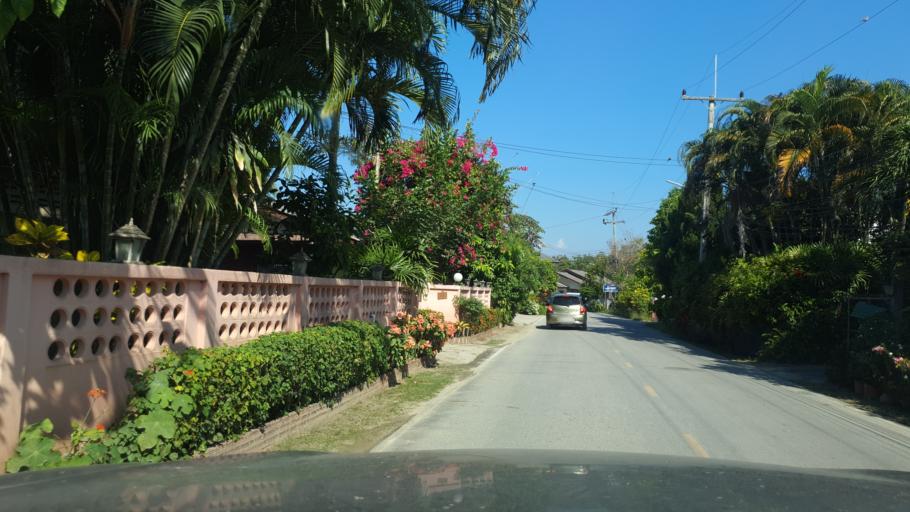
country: TH
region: Chiang Mai
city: San Sai
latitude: 18.8191
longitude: 99.0843
